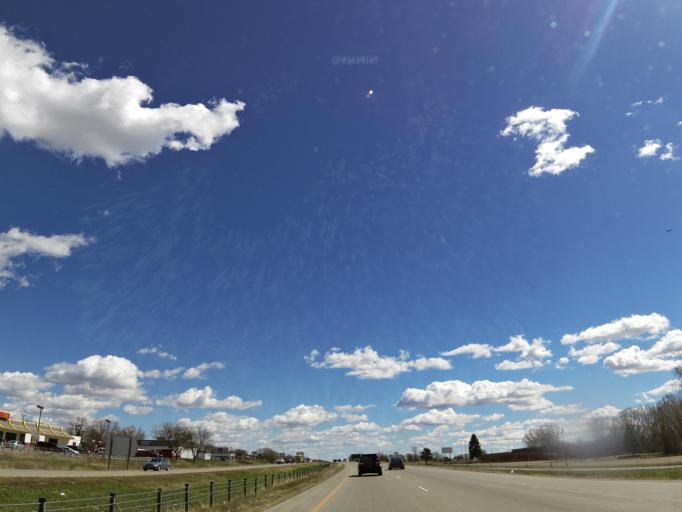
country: US
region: Minnesota
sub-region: Washington County
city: Cottage Grove
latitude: 44.8296
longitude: -92.9604
